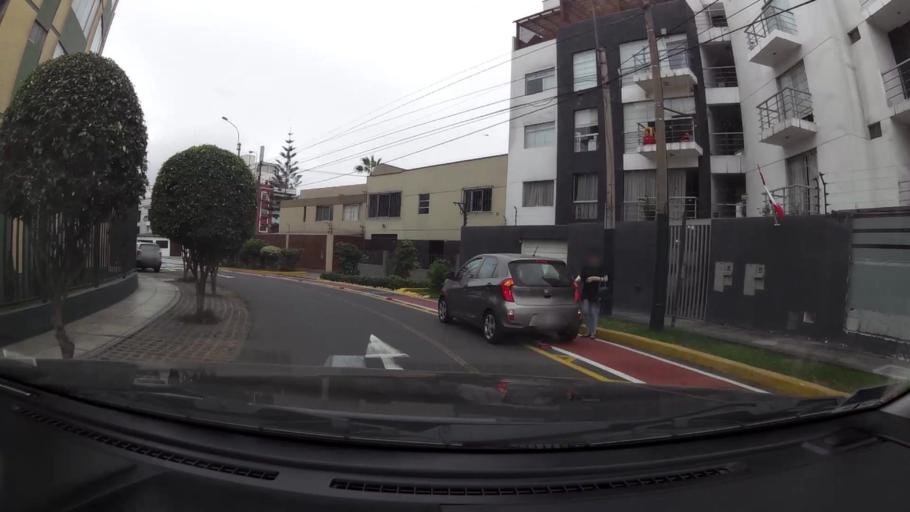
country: PE
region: Lima
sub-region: Lima
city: Surco
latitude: -12.1310
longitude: -76.9985
